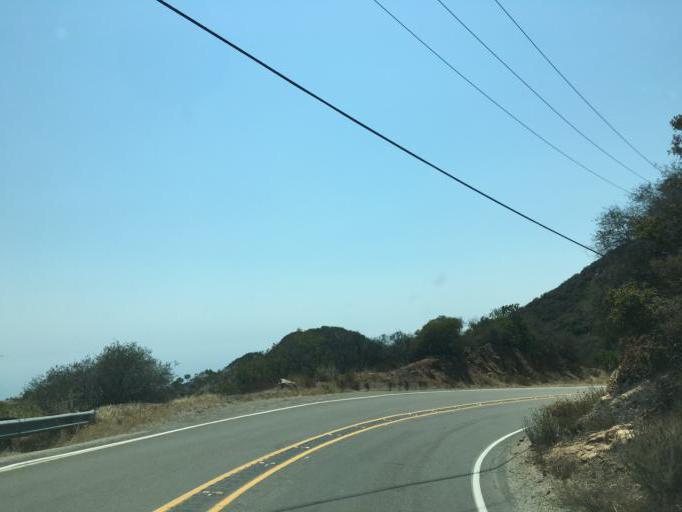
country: US
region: California
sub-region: Los Angeles County
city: Las Flores
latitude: 34.0733
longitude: -118.6515
